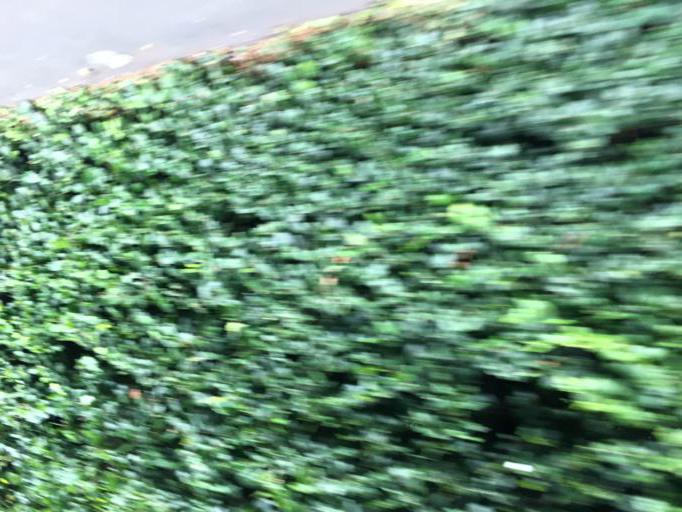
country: GB
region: England
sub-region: Warwickshire
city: Dunchurch
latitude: 52.3557
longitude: -1.2835
